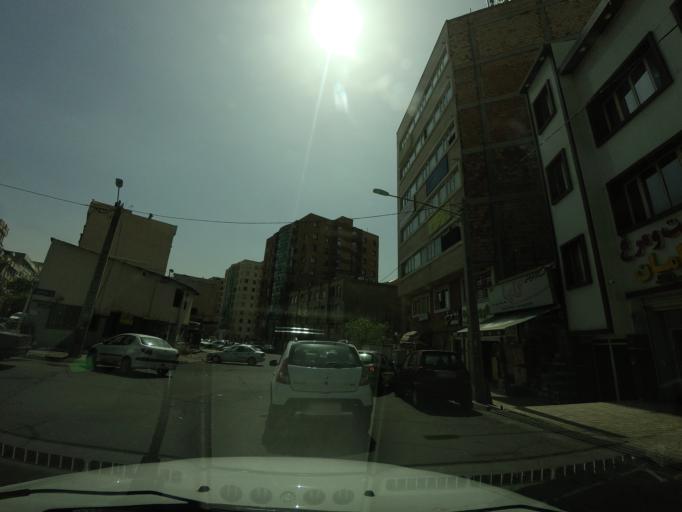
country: IR
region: Tehran
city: Tajrish
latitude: 35.7732
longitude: 51.3276
